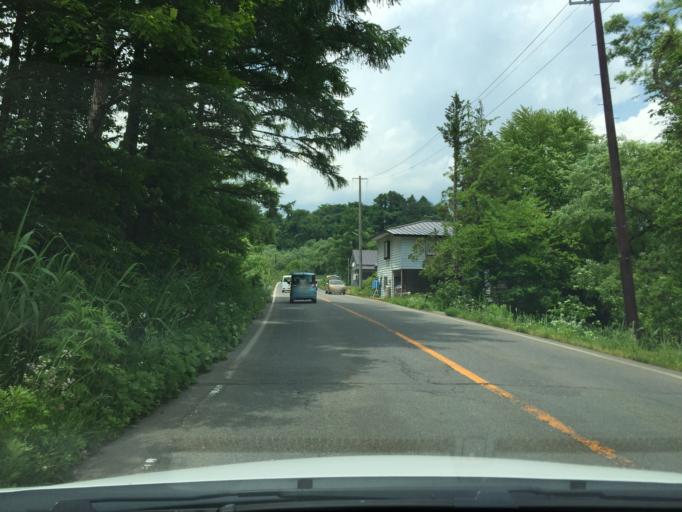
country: JP
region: Fukushima
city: Inawashiro
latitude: 37.6438
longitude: 140.0996
